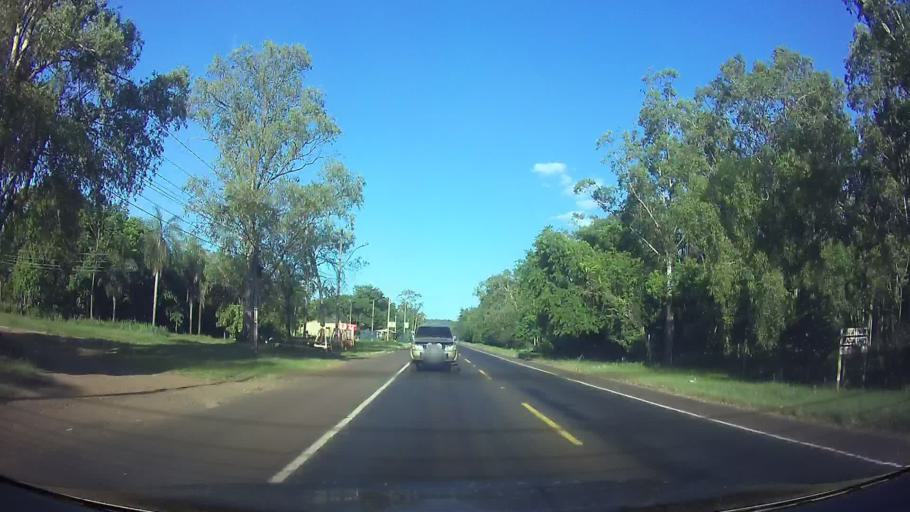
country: PY
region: Central
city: Ypacarai
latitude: -25.3757
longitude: -57.2307
